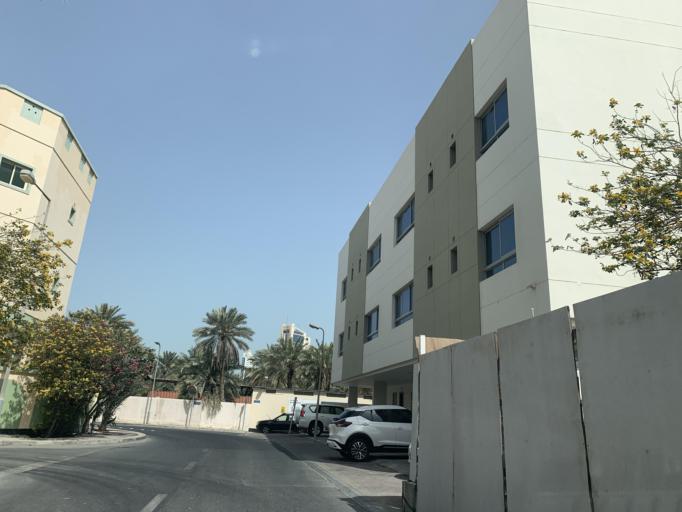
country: BH
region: Manama
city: Jidd Hafs
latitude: 26.2199
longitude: 50.5605
